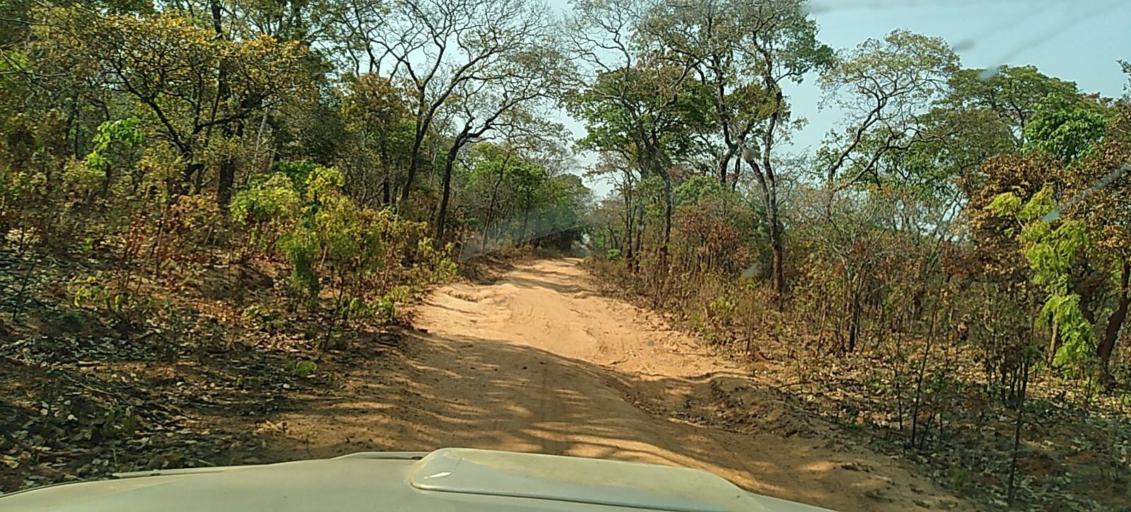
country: ZM
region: North-Western
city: Kasempa
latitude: -13.5322
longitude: 26.4083
